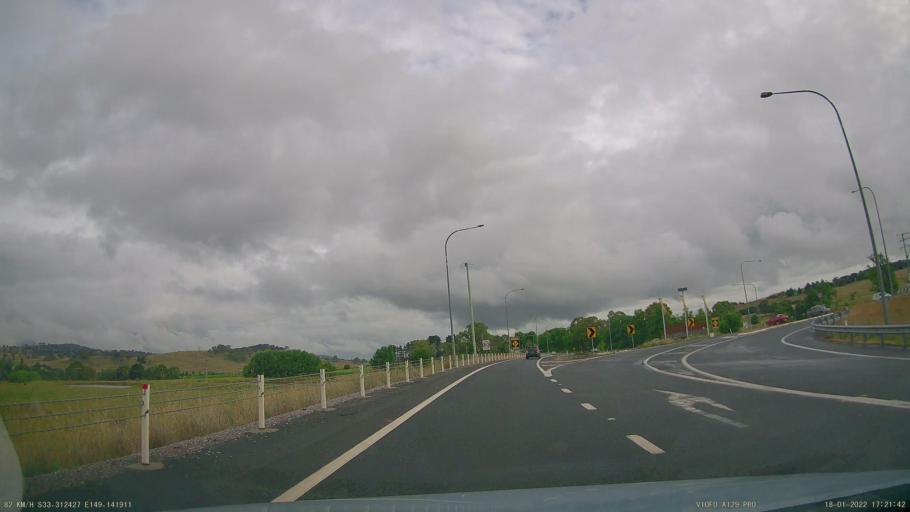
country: AU
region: New South Wales
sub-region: Orange Municipality
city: Orange
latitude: -33.3126
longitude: 149.1420
